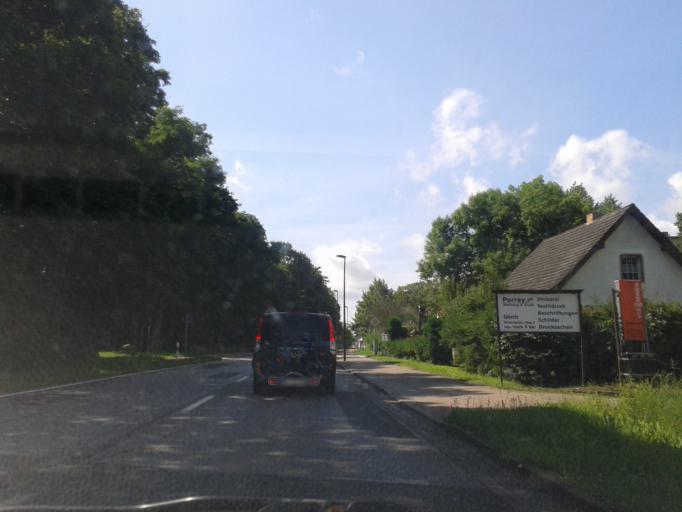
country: DE
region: Mecklenburg-Vorpommern
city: Pasewalk
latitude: 53.4751
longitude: 13.9804
